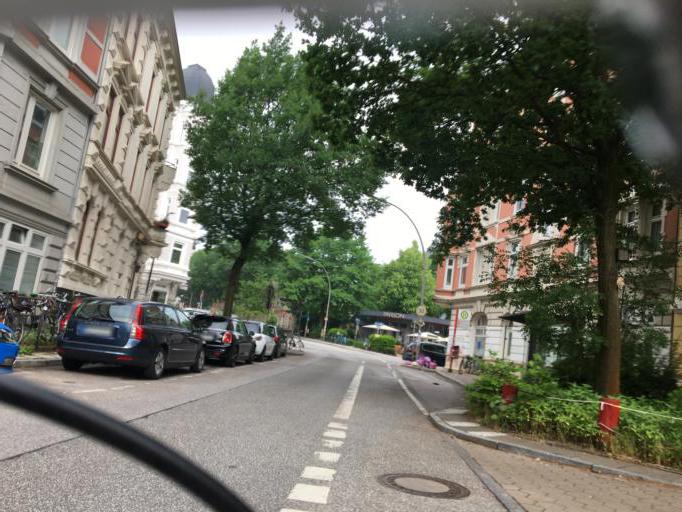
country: DE
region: Hamburg
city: Altona
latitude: 53.5506
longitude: 9.9262
